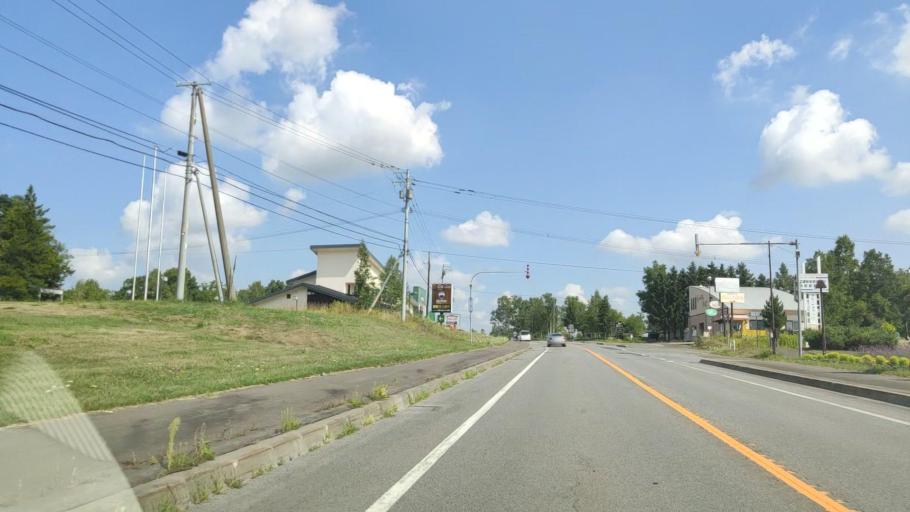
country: JP
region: Hokkaido
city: Shimo-furano
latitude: 43.5177
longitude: 142.4479
